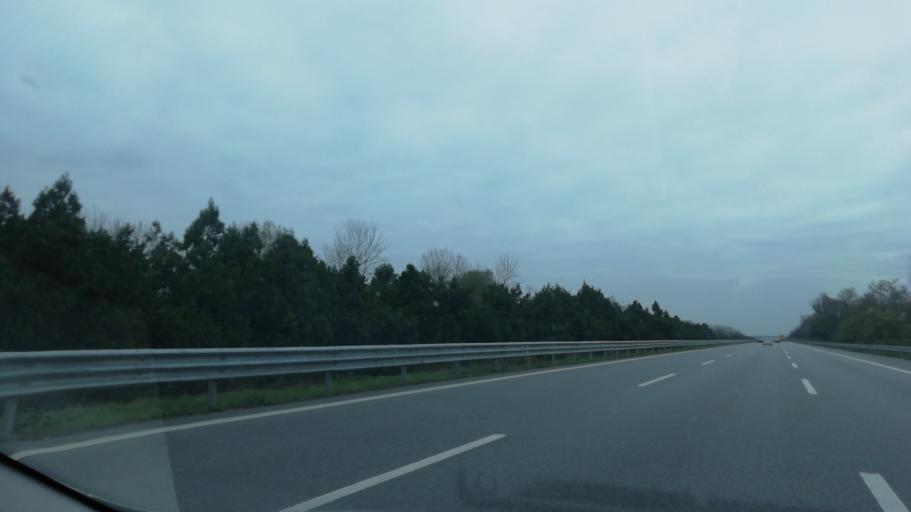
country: TR
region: Duzce
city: Cilimli
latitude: 40.8230
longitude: 31.0633
